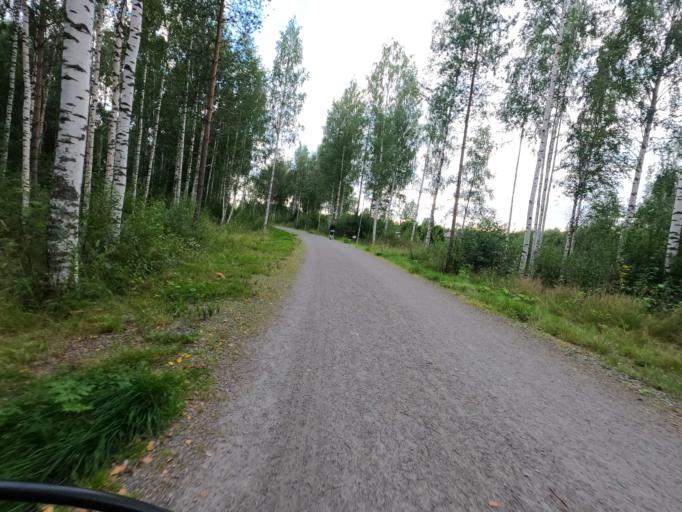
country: FI
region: North Karelia
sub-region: Joensuu
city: Joensuu
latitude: 62.6139
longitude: 29.8540
